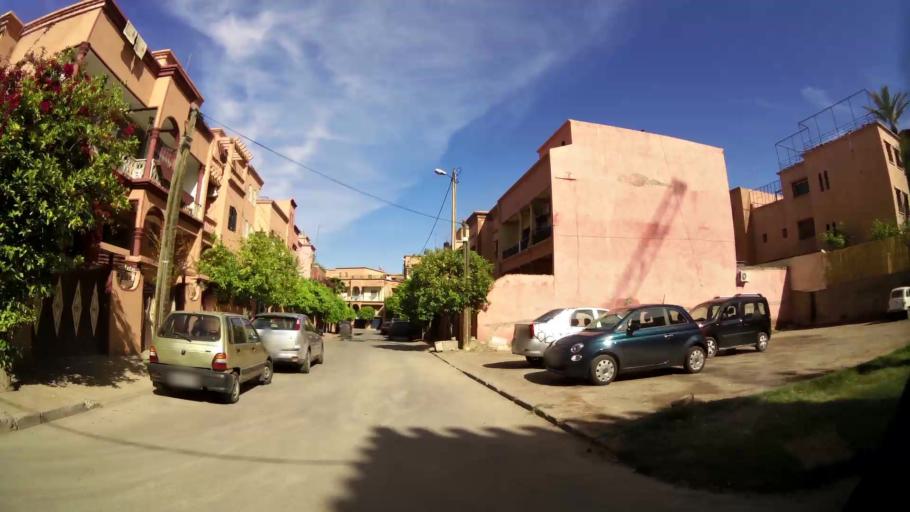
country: MA
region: Marrakech-Tensift-Al Haouz
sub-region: Marrakech
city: Marrakesh
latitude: 31.6458
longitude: -8.0092
